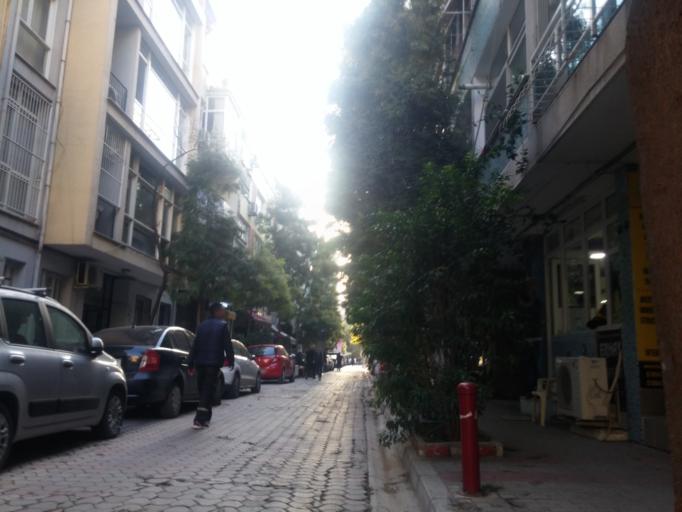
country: TR
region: Izmir
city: Izmir
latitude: 38.4333
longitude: 27.1395
